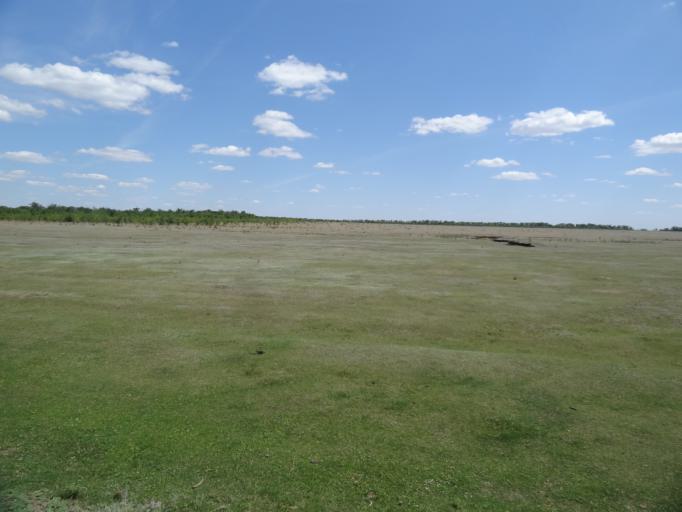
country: RU
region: Saratov
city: Sovetskoye
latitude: 51.2904
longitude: 46.6571
